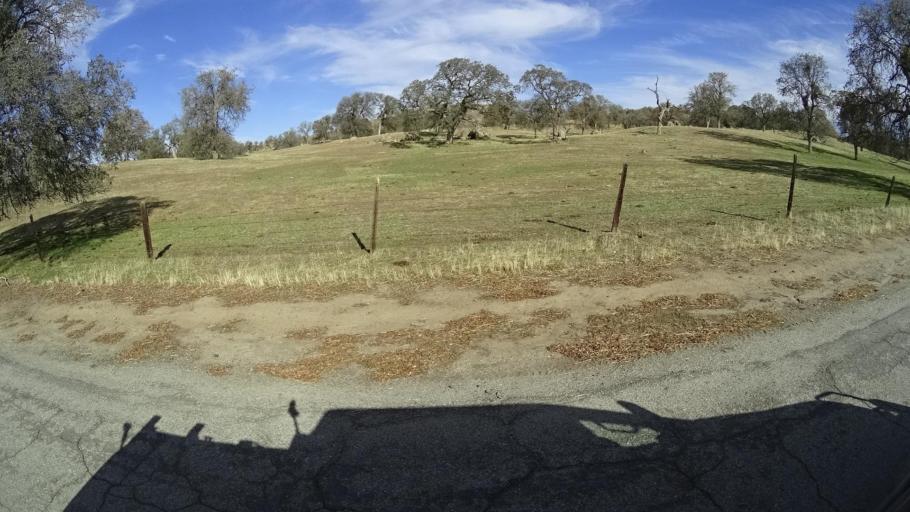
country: US
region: California
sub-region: Kern County
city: Oildale
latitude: 35.5824
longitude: -118.8220
